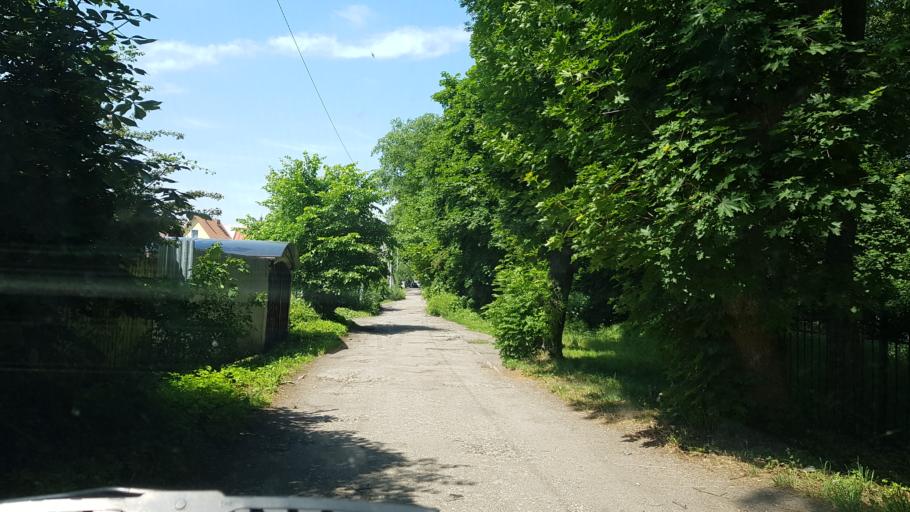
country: RU
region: Kaliningrad
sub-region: Gorod Kaliningrad
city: Baltiysk
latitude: 54.6483
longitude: 19.8907
